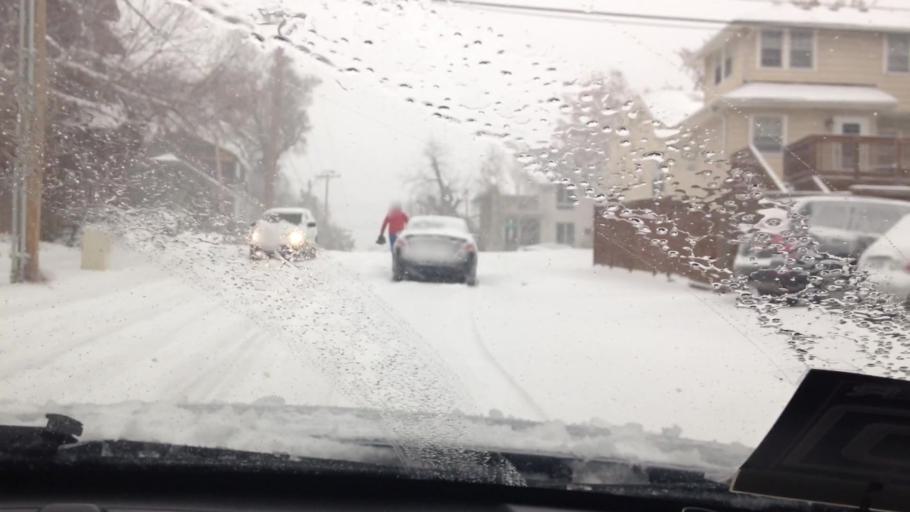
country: US
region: Kansas
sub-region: Johnson County
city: Westwood
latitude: 39.0409
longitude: -94.6033
